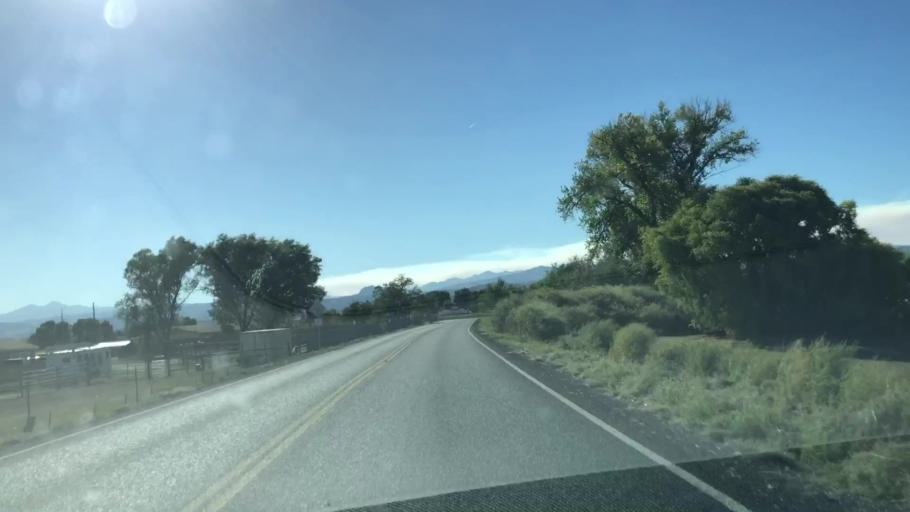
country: US
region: Colorado
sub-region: Larimer County
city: Loveland
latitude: 40.4609
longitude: -105.0505
